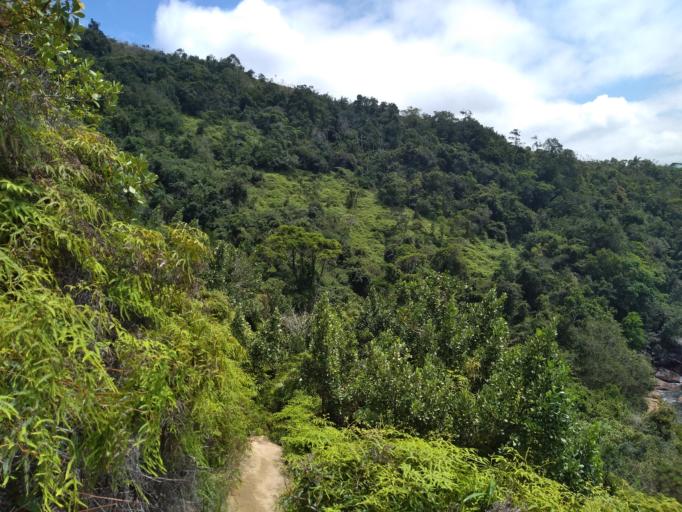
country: BR
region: Sao Paulo
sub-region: Ubatuba
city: Ubatuba
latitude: -23.5350
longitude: -45.1592
